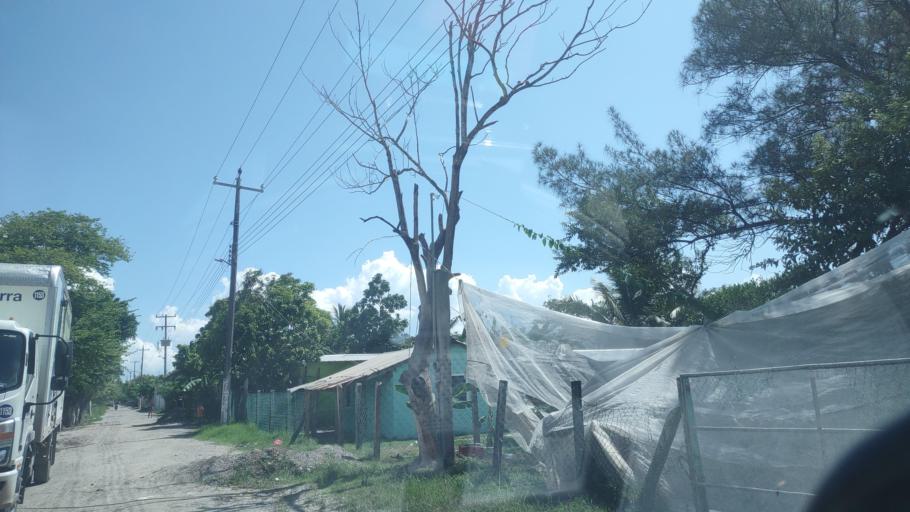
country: MX
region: Veracruz
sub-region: Ozuluama de Mascarenas
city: Cucharas
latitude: 21.6182
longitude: -97.6547
